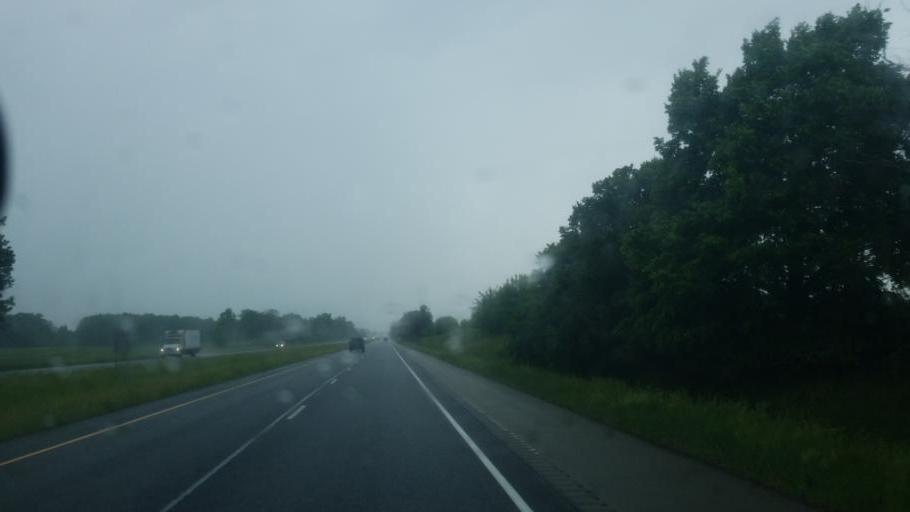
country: US
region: Indiana
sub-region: Whitley County
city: Columbia City
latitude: 41.1334
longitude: -85.4038
